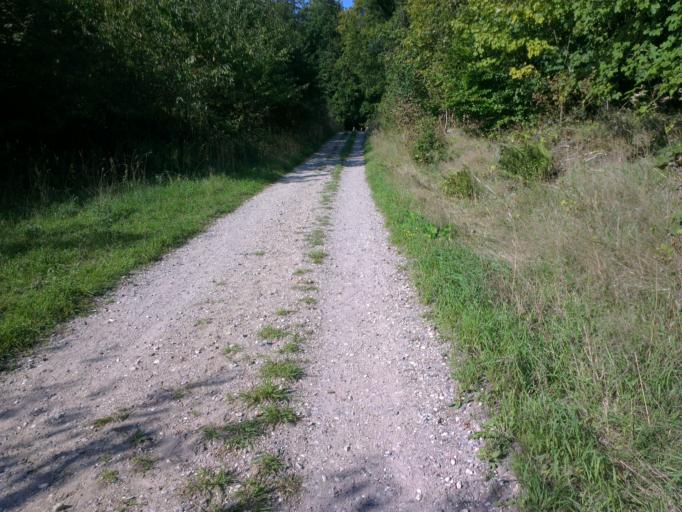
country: DK
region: Capital Region
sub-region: Frederikssund Kommune
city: Frederikssund
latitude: 55.8413
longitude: 12.0239
